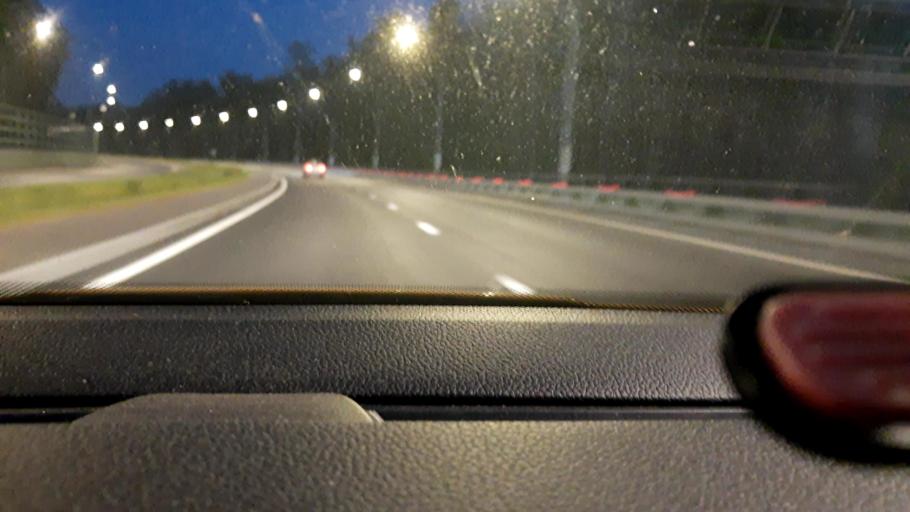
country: RU
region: Moskovskaya
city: Moskovskiy
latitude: 55.5865
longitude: 37.3997
